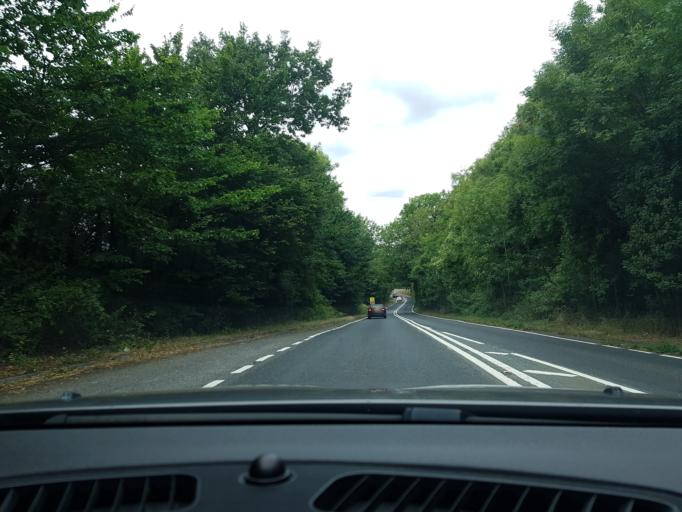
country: GB
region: England
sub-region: Hampshire
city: Kingsclere
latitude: 51.3178
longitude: -1.2093
